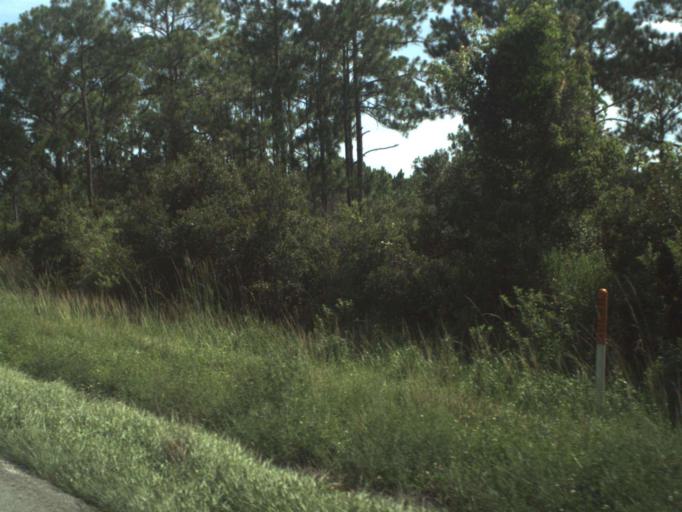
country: US
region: Florida
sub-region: Indian River County
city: Fellsmere
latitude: 27.7162
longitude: -80.5436
